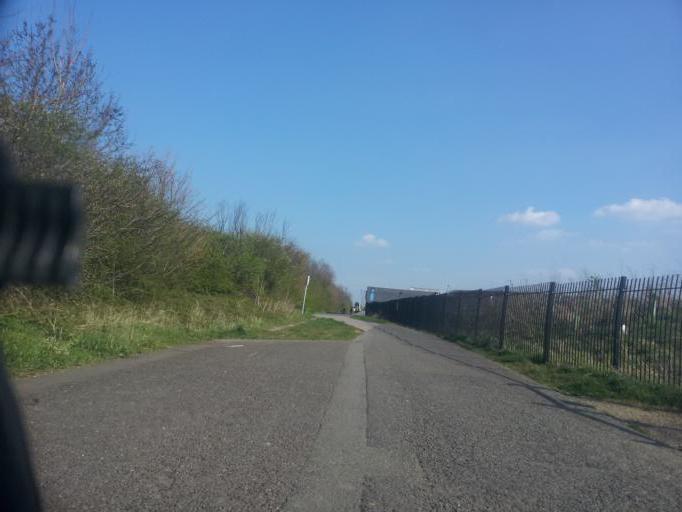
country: GB
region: England
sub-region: Kent
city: Gravesend
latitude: 51.4200
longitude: 0.3524
